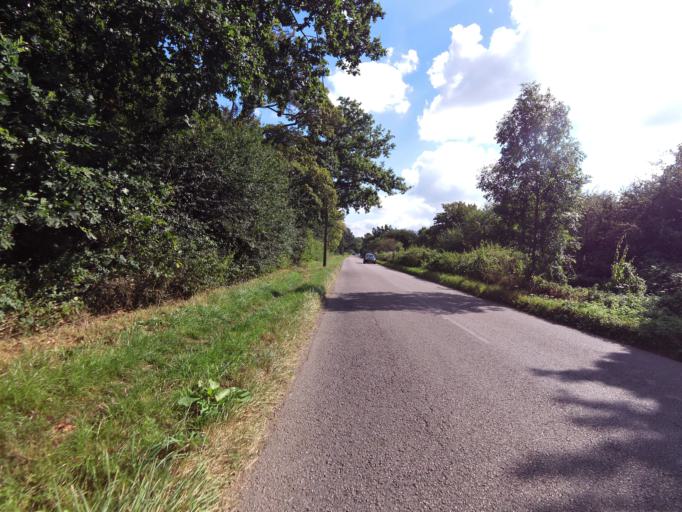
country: GB
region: England
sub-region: Greater London
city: High Barnet
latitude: 51.6629
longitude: -0.2299
